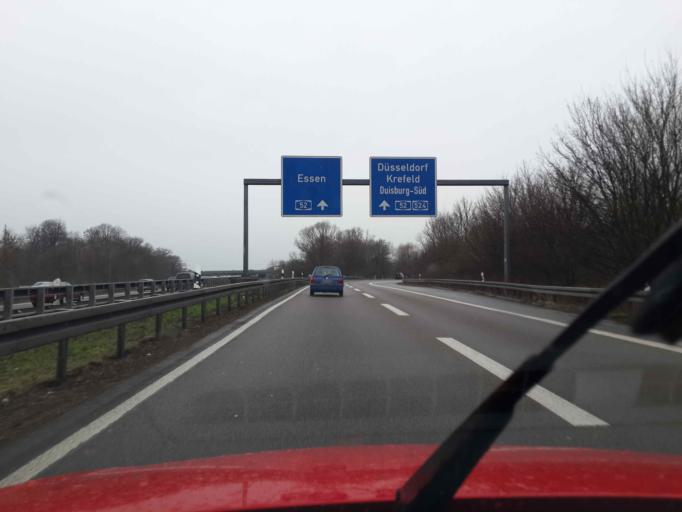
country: DE
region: North Rhine-Westphalia
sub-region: Regierungsbezirk Dusseldorf
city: Ratingen
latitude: 51.3475
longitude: 6.8623
